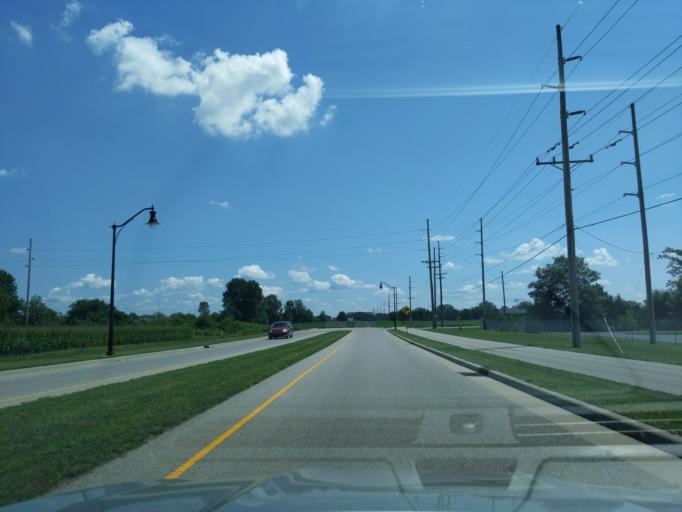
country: US
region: Indiana
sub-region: Decatur County
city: Greensburg
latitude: 39.3586
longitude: -85.4904
